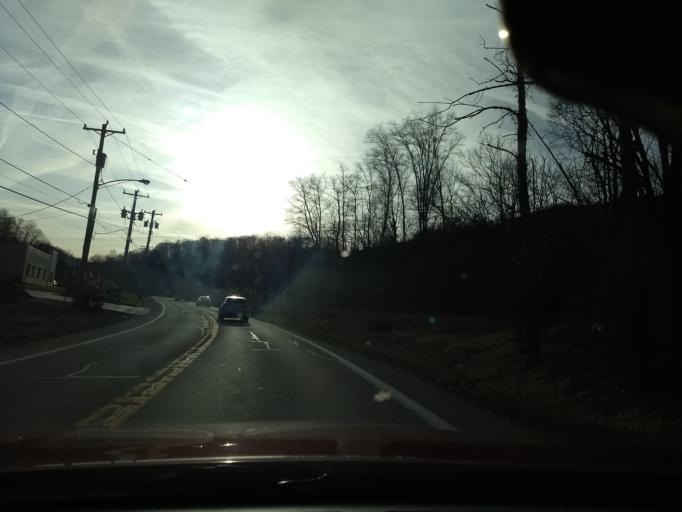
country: US
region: Pennsylvania
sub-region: Allegheny County
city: Brentwood
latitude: 40.3745
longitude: -79.9422
